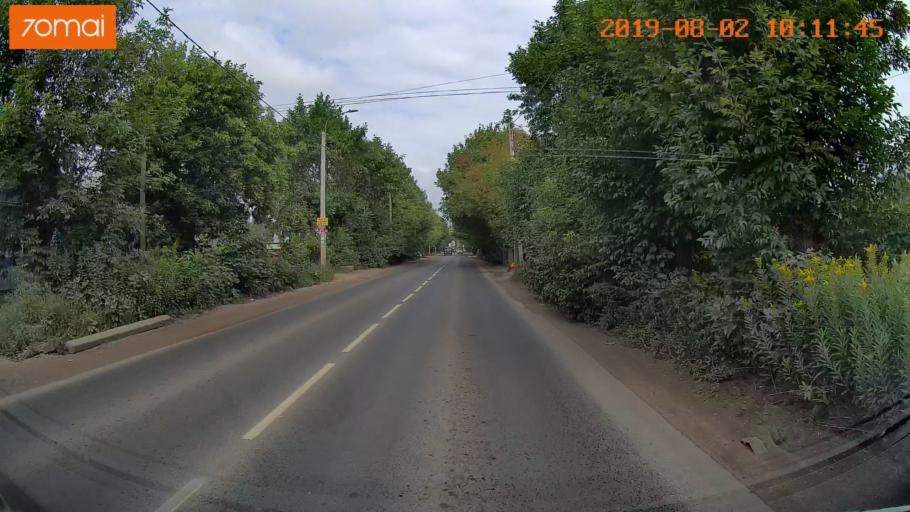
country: RU
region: Ivanovo
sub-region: Gorod Ivanovo
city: Ivanovo
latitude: 56.9949
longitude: 40.9518
